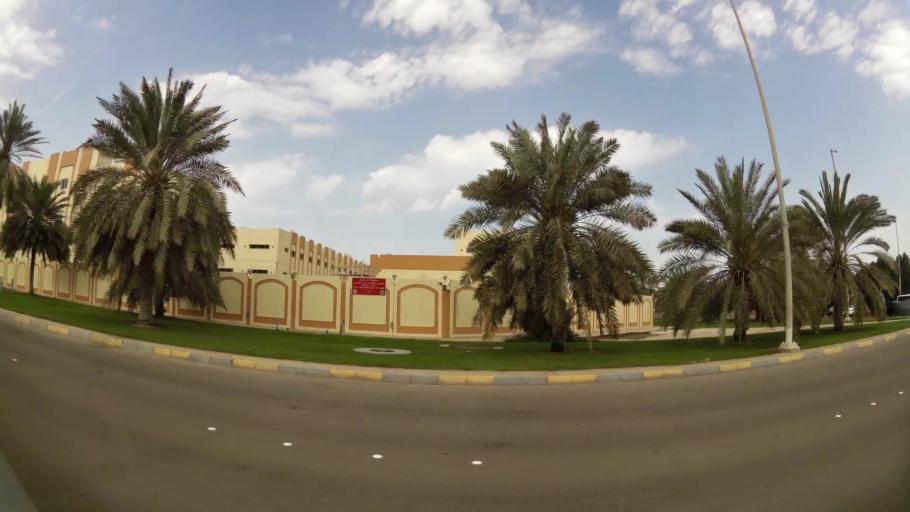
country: AE
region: Abu Dhabi
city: Abu Dhabi
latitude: 24.4474
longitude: 54.3578
